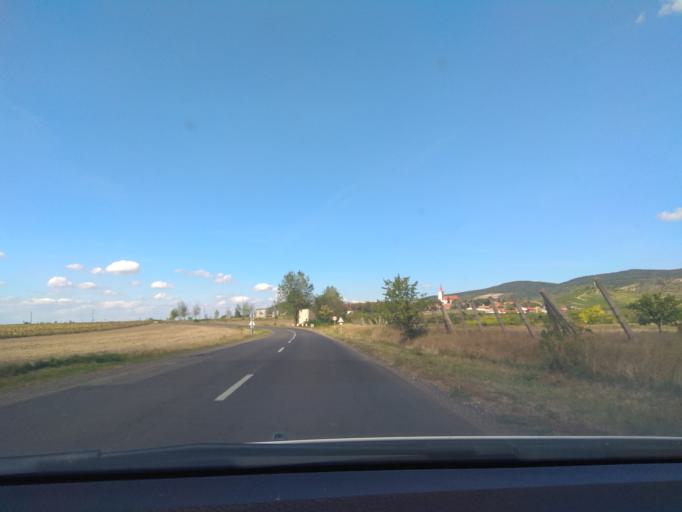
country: HU
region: Borsod-Abauj-Zemplen
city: Tallya
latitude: 48.2254
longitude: 21.2378
